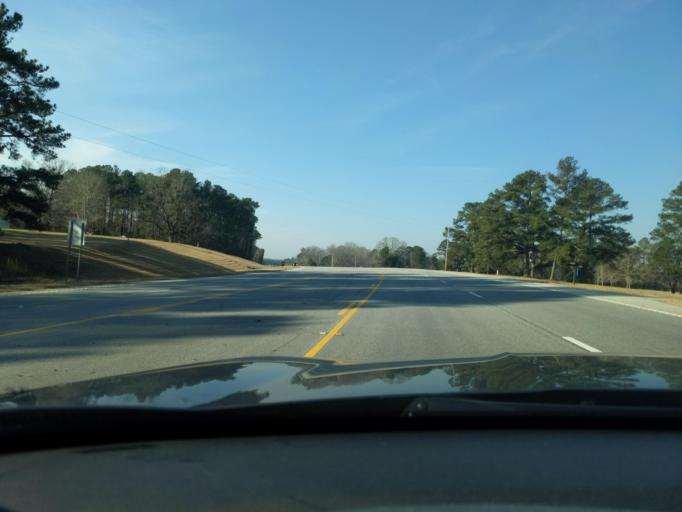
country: US
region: South Carolina
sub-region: Abbeville County
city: Abbeville
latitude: 34.1202
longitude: -82.4566
